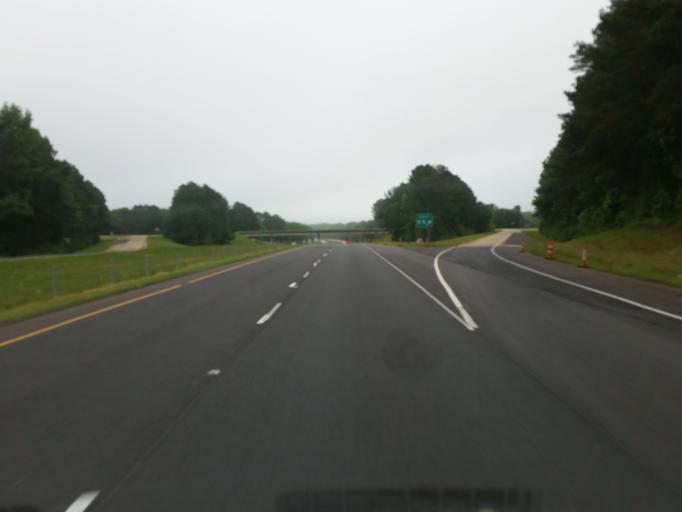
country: US
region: Louisiana
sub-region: Webster Parish
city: Minden
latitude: 32.5635
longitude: -93.1630
